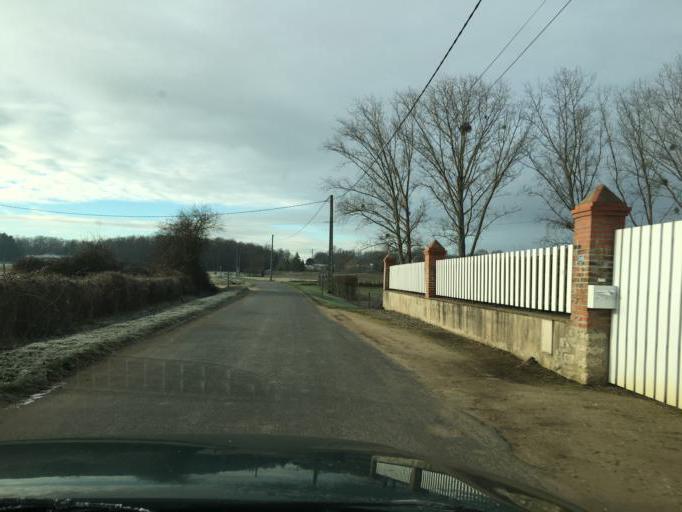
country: FR
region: Centre
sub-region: Departement du Loiret
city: Dry
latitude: 47.8065
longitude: 1.7321
